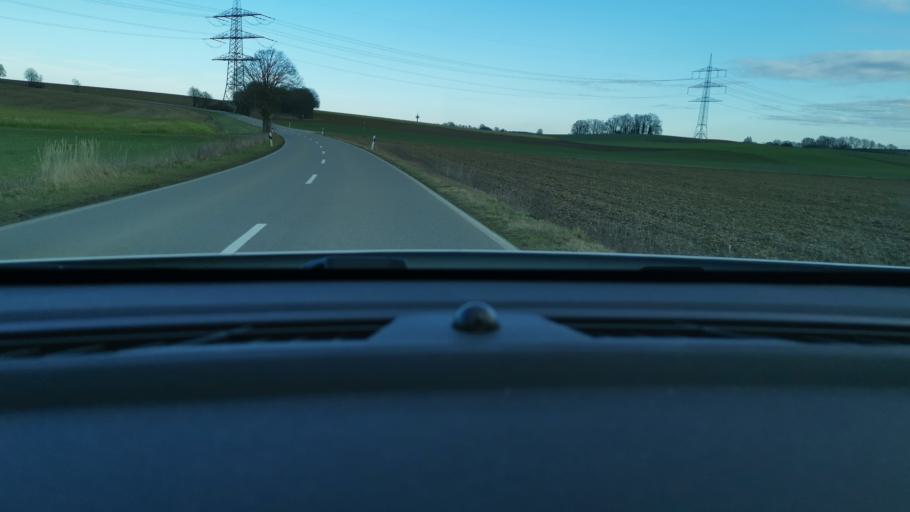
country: DE
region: Bavaria
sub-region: Swabia
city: Affing
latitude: 48.4884
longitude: 10.9688
